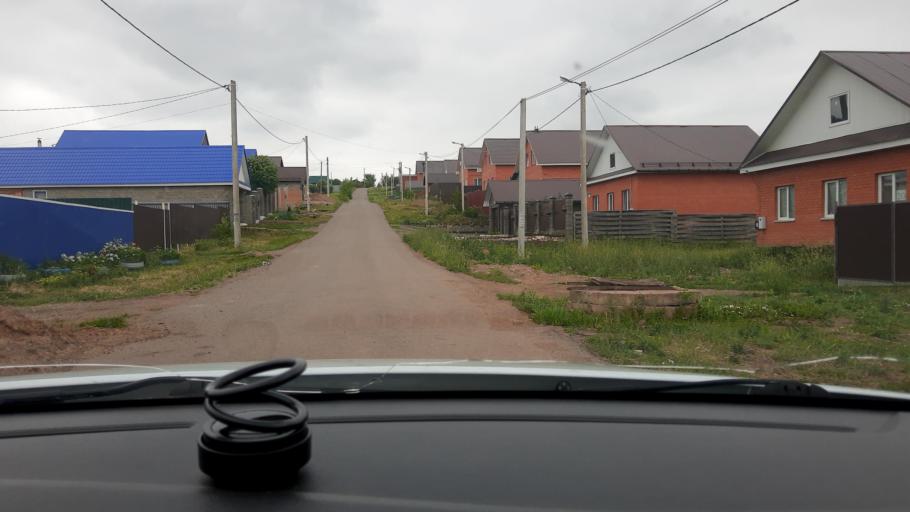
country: RU
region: Bashkortostan
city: Avdon
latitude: 54.6255
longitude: 55.6015
